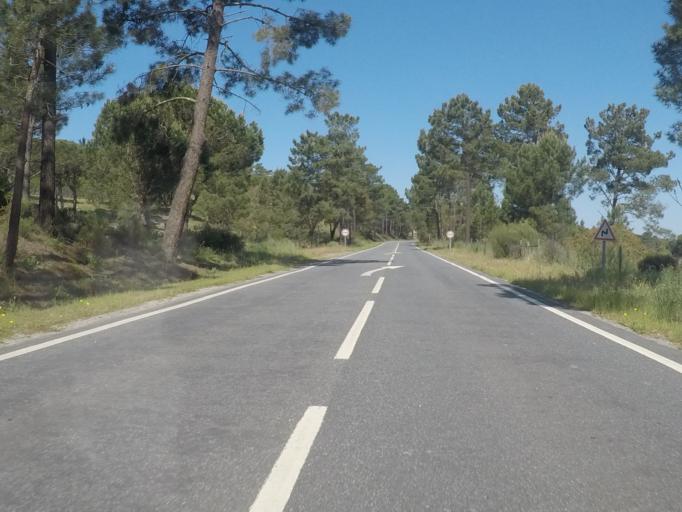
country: PT
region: Setubal
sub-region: Grandola
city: Grandola
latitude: 38.3007
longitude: -8.7310
